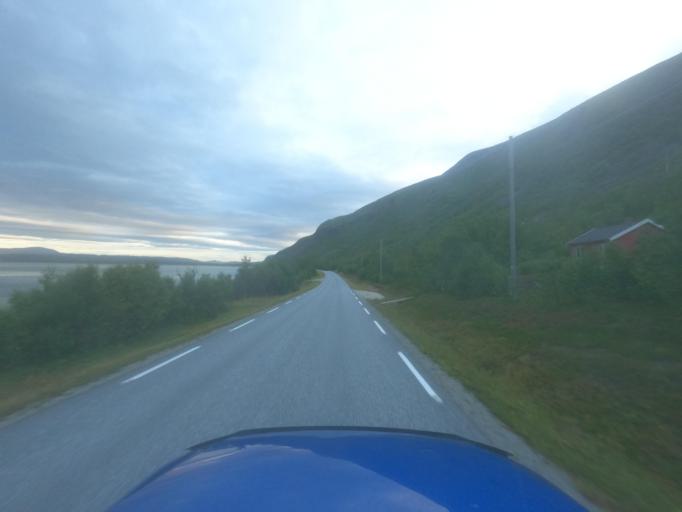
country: NO
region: Finnmark Fylke
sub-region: Porsanger
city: Lakselv
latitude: 70.1008
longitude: 24.9133
